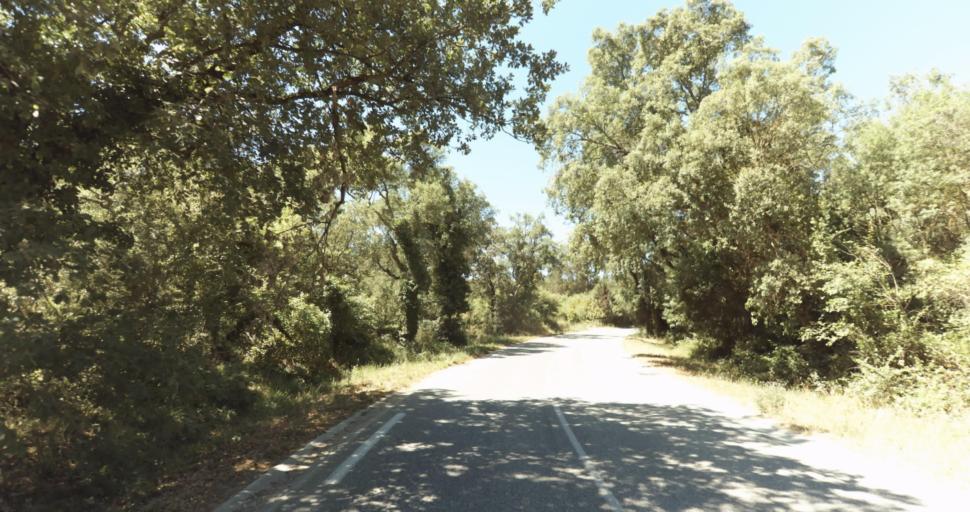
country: FR
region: Provence-Alpes-Cote d'Azur
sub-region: Departement du Var
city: Gassin
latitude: 43.2480
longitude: 6.5803
